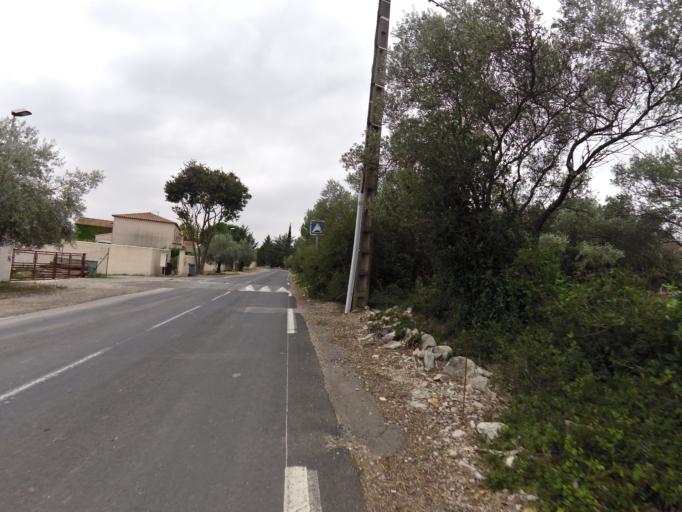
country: FR
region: Languedoc-Roussillon
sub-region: Departement de l'Herault
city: Villetelle
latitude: 43.7253
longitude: 4.1328
